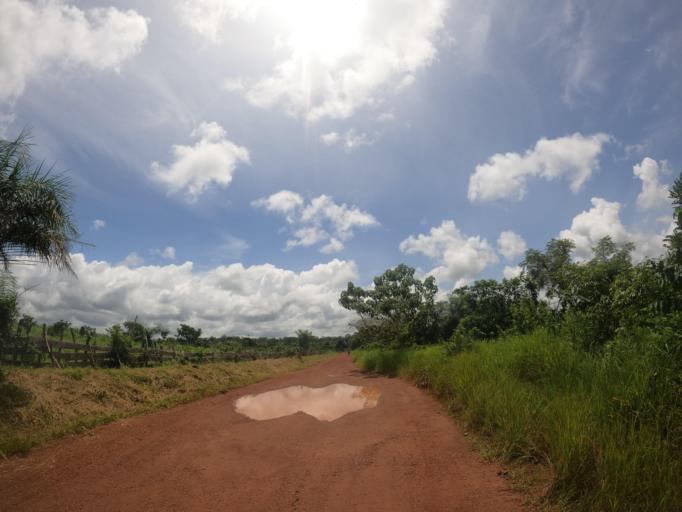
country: SL
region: Northern Province
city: Makeni
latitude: 9.1320
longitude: -12.2420
